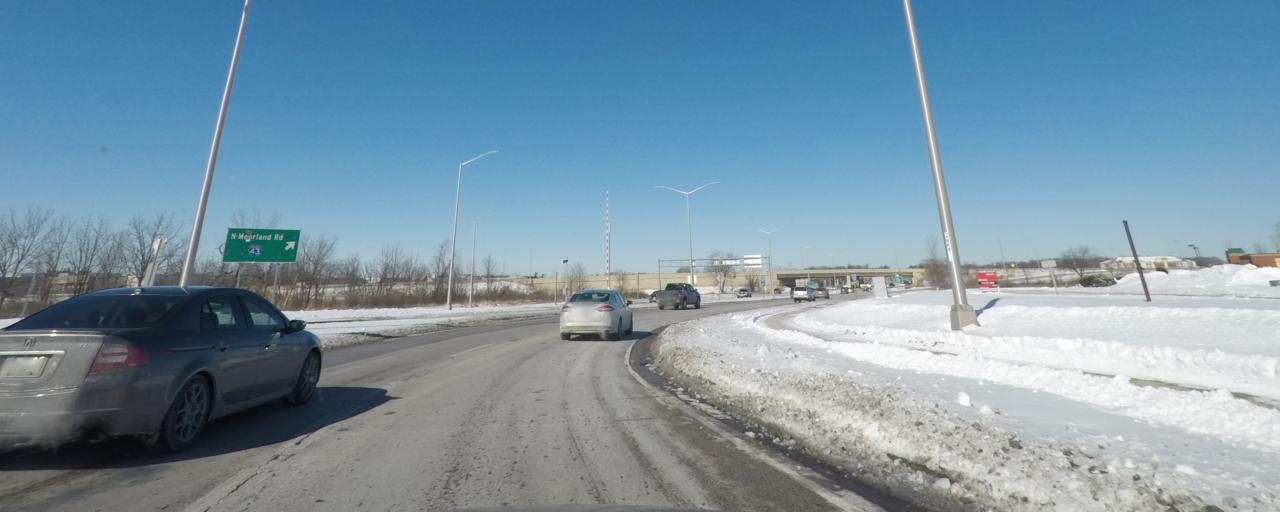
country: US
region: Wisconsin
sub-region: Waukesha County
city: New Berlin
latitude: 42.9493
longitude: -88.1087
